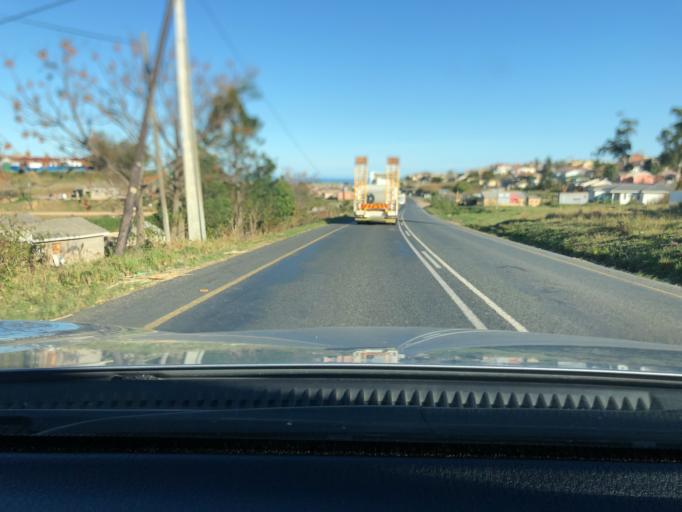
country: ZA
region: KwaZulu-Natal
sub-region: eThekwini Metropolitan Municipality
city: Umkomaas
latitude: -30.0051
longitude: 30.8025
